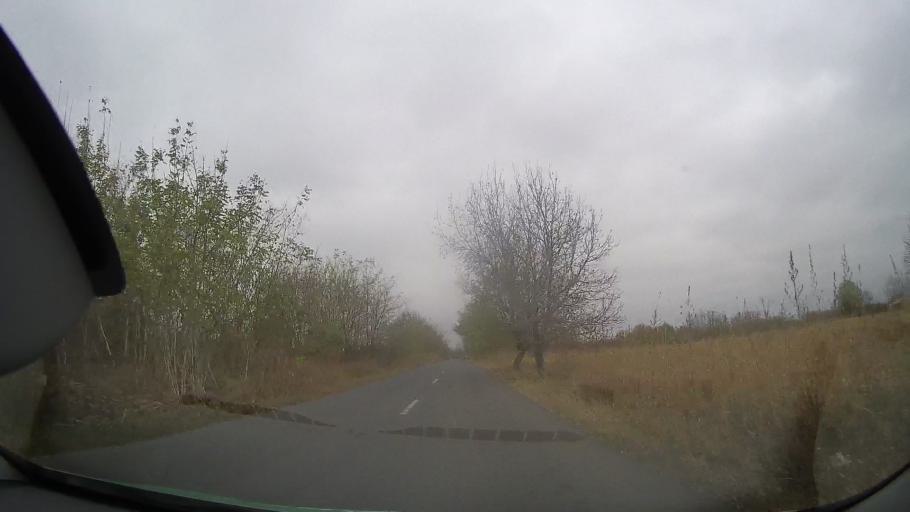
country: RO
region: Buzau
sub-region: Comuna Bradeanu
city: Bradeanu
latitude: 44.9187
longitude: 26.8679
